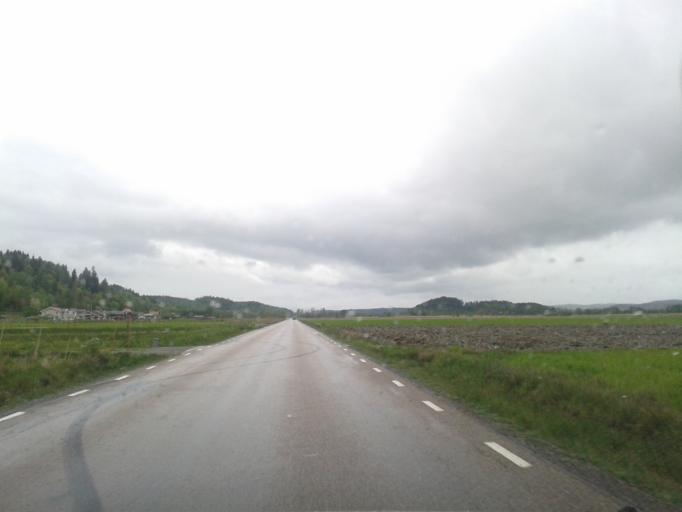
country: SE
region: Vaestra Goetaland
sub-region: Ale Kommun
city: Alvangen
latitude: 57.9847
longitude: 12.1145
